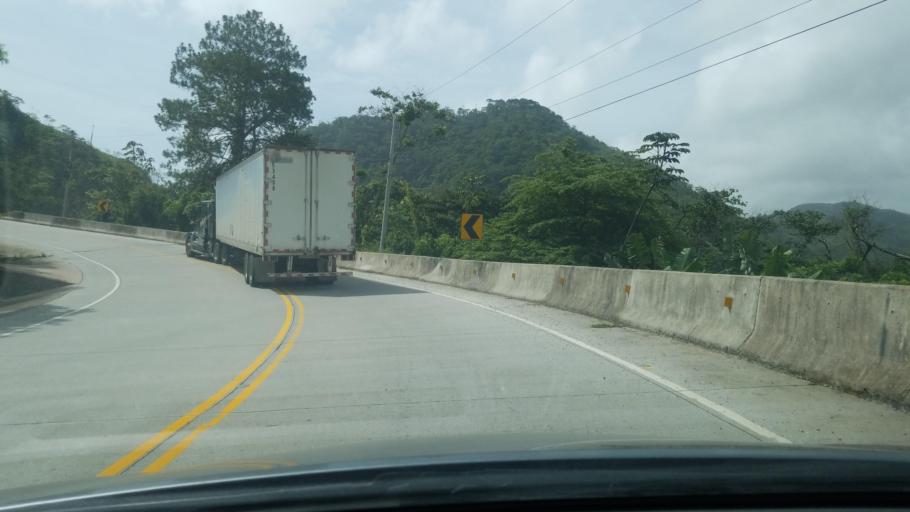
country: HN
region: Copan
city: San Jeronimo
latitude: 14.9319
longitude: -88.9529
